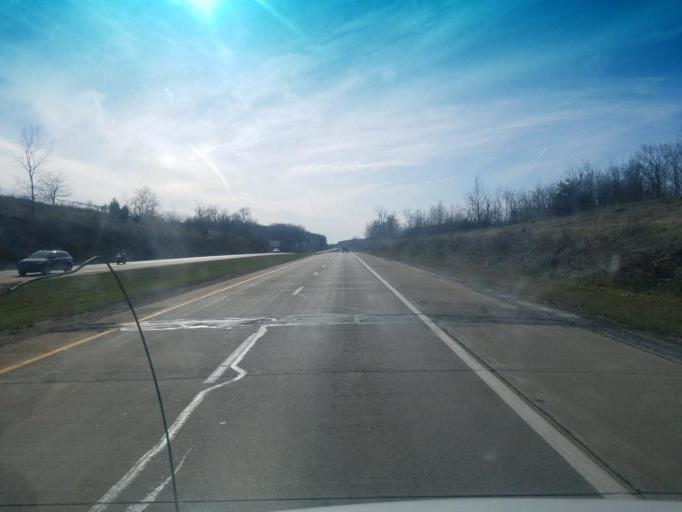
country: US
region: Ohio
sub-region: Champaign County
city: North Lewisburg
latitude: 40.3247
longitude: -83.5972
